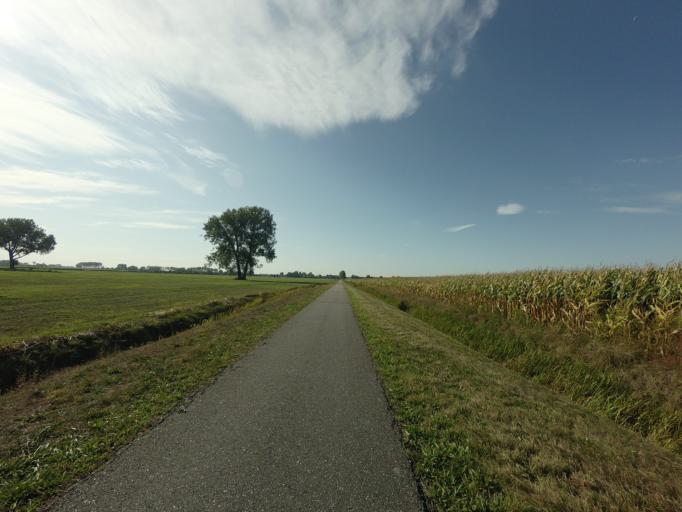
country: NL
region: South Holland
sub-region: Gemeente Leerdam
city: Leerdam
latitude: 51.9280
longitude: 5.0769
